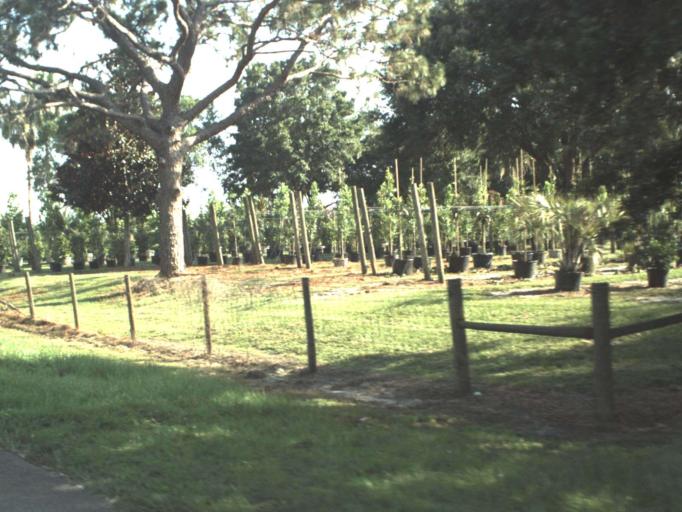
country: US
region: Florida
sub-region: Lake County
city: Groveland
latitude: 28.5015
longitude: -81.8373
